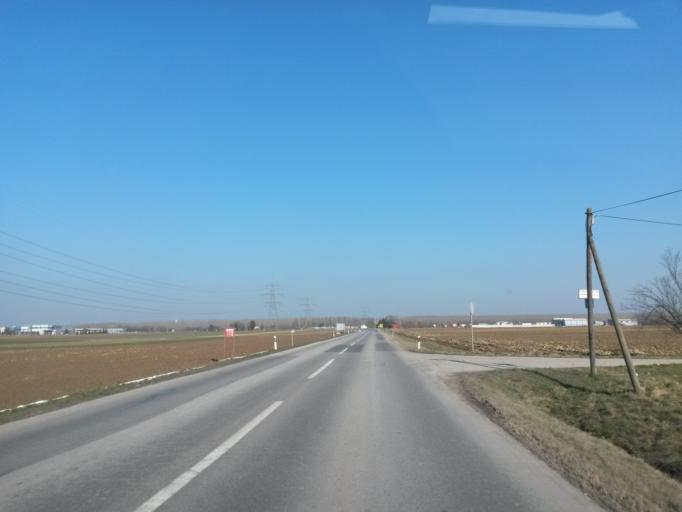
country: HR
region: Osjecko-Baranjska
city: Josipovac
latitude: 45.5892
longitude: 18.5631
